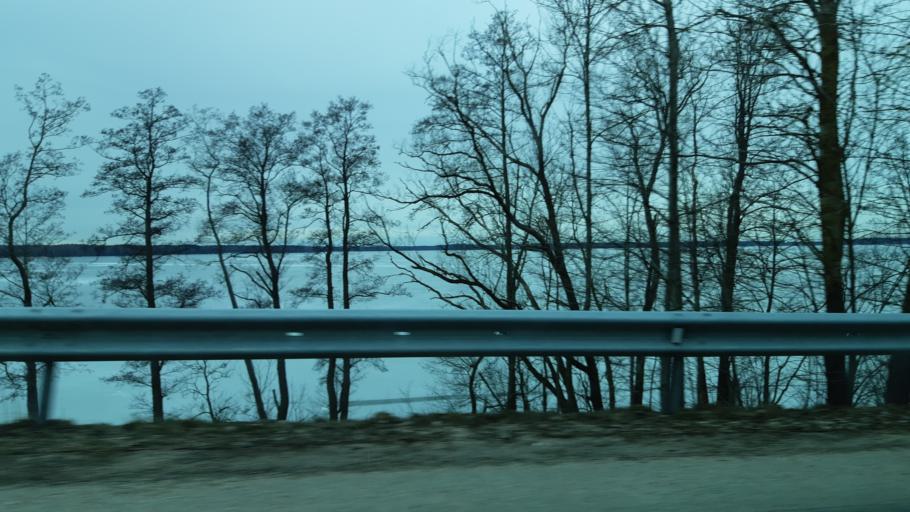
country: LT
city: Virbalis
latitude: 54.4129
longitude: 22.7598
